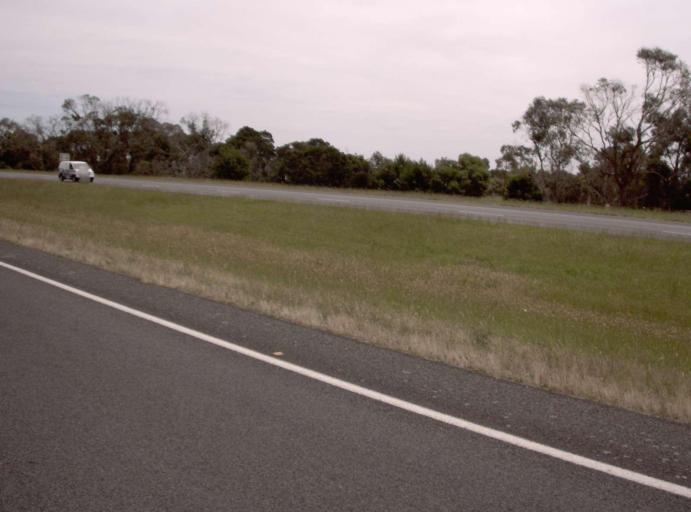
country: AU
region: Victoria
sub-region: Mornington Peninsula
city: Safety Beach
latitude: -38.3256
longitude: 144.9980
